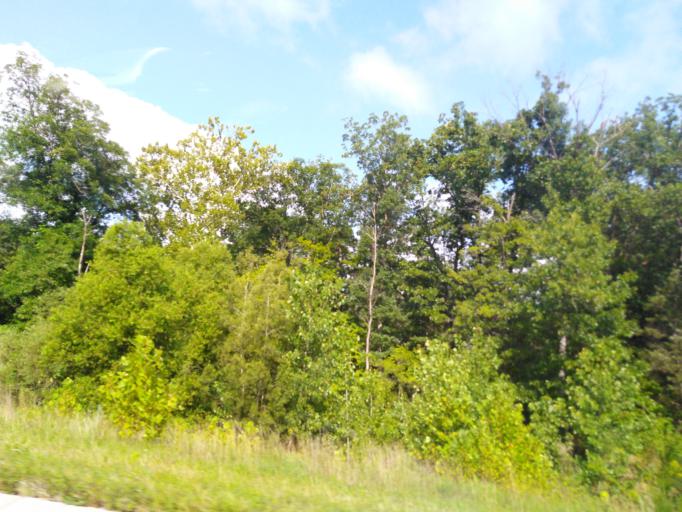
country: US
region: Missouri
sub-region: Jefferson County
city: Hillsboro
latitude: 38.2774
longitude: -90.5523
